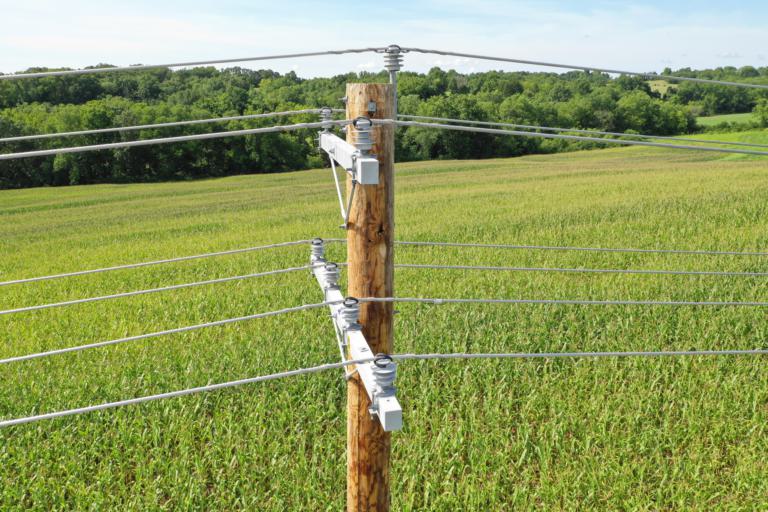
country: US
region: Missouri
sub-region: Callaway County
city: Holts Summit
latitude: 38.5324
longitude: -92.0415
